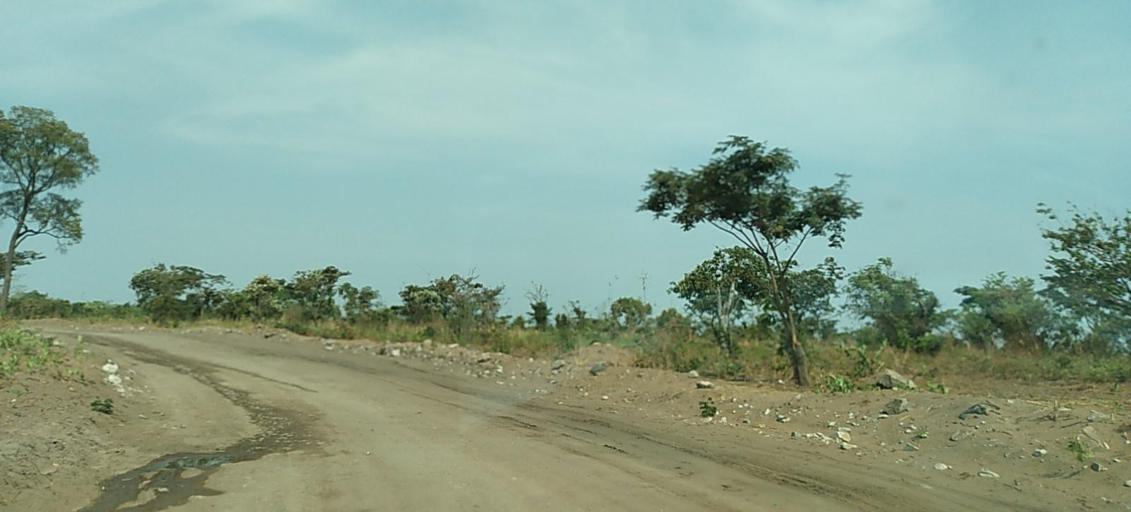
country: ZM
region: Copperbelt
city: Chililabombwe
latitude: -12.2917
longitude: 27.7641
